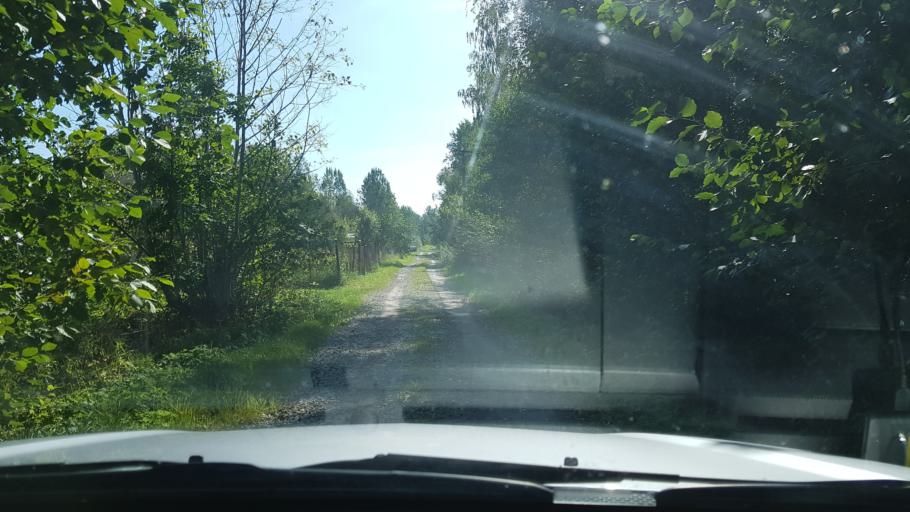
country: EE
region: Ida-Virumaa
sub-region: Sillamaee linn
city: Sillamae
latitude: 59.3176
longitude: 27.7845
